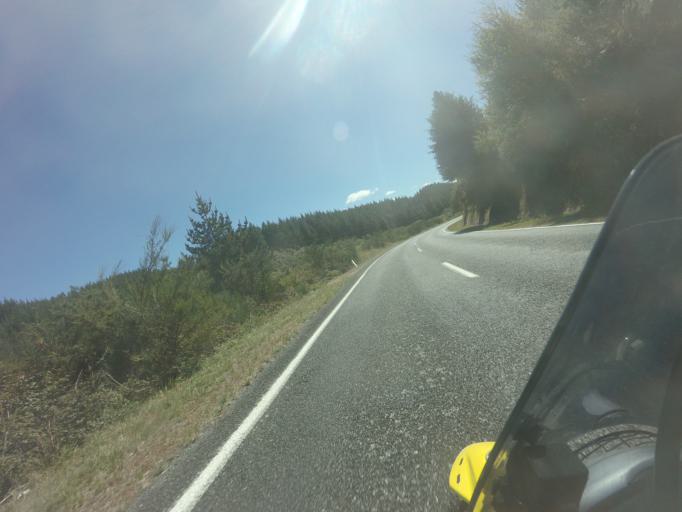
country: NZ
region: Bay of Plenty
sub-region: Whakatane District
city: Murupara
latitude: -38.2987
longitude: 176.8144
